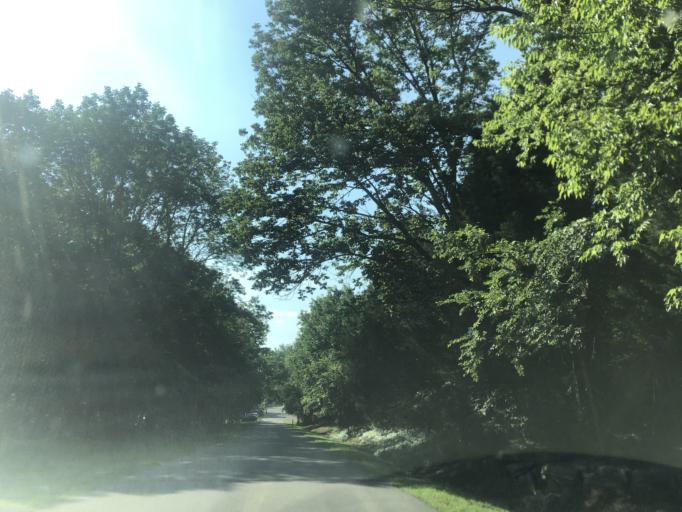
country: US
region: Tennessee
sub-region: Wilson County
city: Green Hill
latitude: 36.1377
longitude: -86.6010
